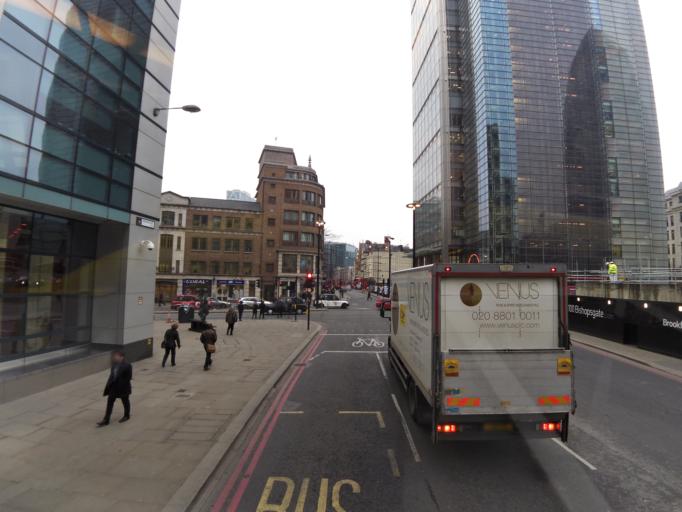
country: GB
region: England
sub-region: Greater London
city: City of London
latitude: 51.5158
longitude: -0.0821
